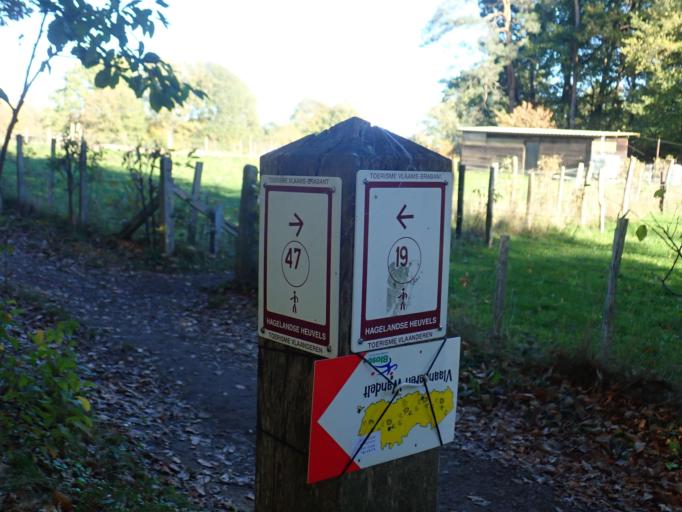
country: BE
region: Flanders
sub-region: Provincie Vlaams-Brabant
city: Holsbeek
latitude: 50.8993
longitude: 4.7496
